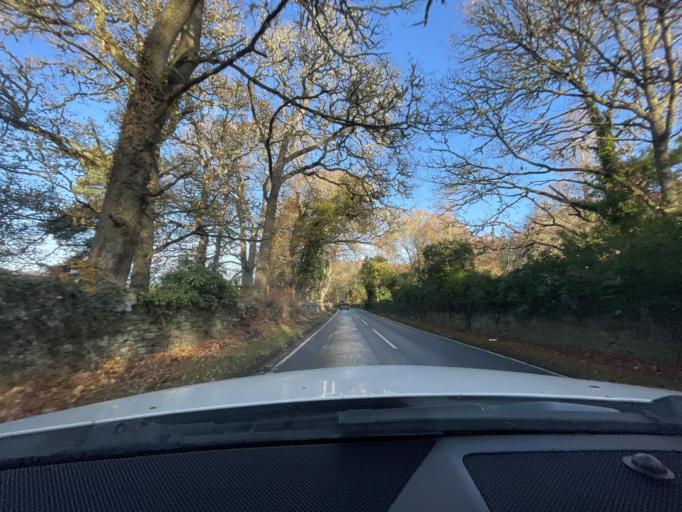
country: GB
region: Scotland
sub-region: Highland
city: Inverness
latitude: 57.4441
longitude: -4.2596
